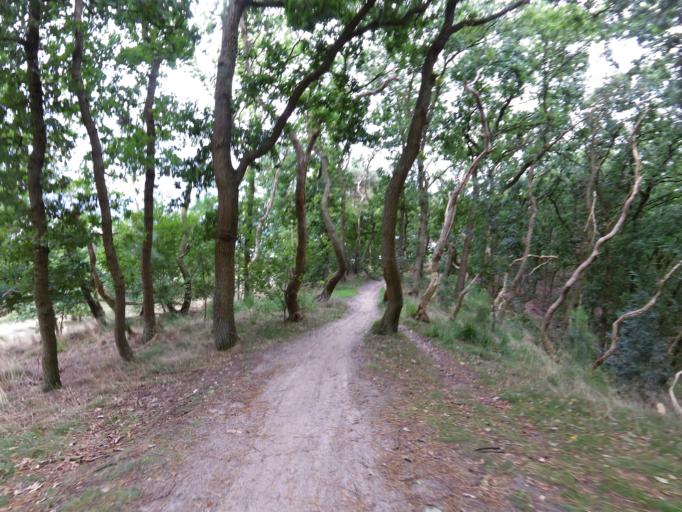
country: NL
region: North Brabant
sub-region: Gemeente Waalwijk
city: Waalwijk
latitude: 51.6564
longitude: 5.0867
